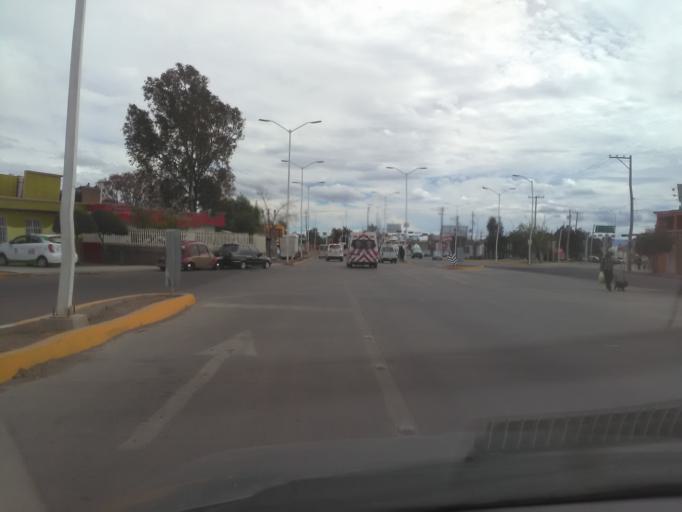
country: MX
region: Durango
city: Victoria de Durango
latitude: 24.0376
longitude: -104.6778
